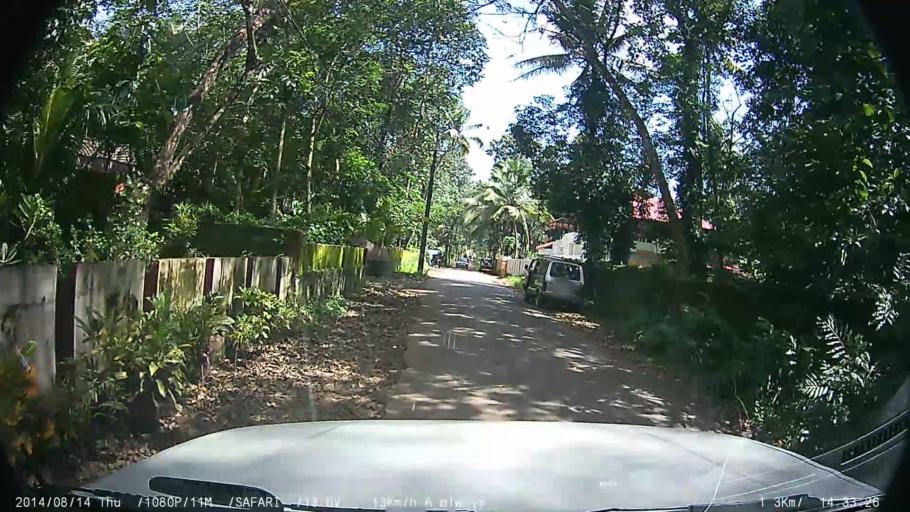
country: IN
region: Kerala
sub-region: Kottayam
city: Kottayam
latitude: 9.5321
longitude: 76.5331
